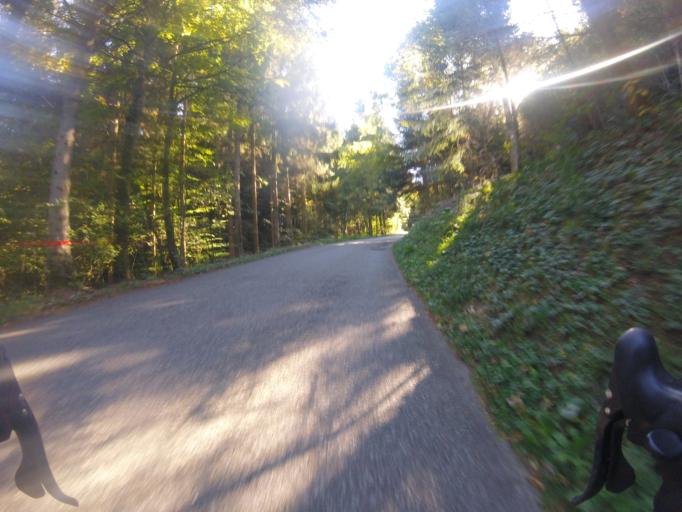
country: CH
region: Bern
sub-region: Seeland District
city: Schupfen
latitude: 47.0302
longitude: 7.3918
